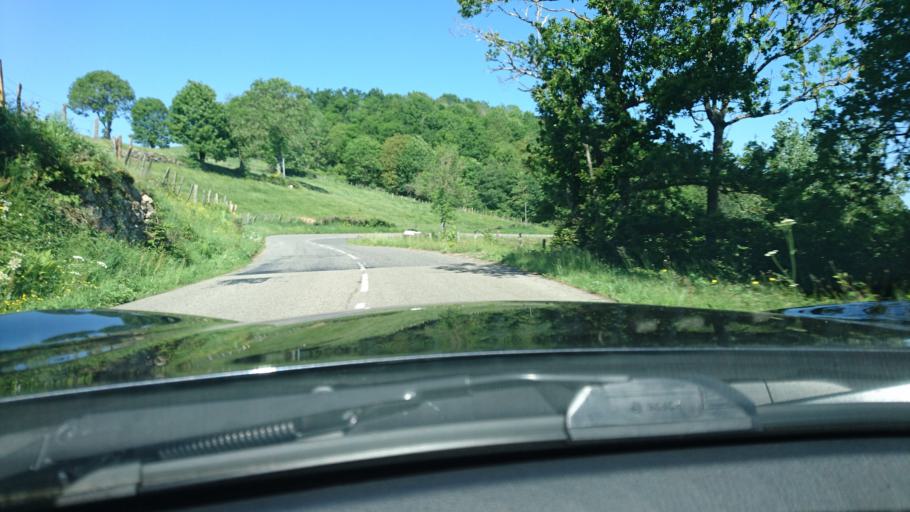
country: FR
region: Rhone-Alpes
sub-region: Departement du Rhone
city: Montrottier
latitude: 45.7981
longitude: 4.4361
